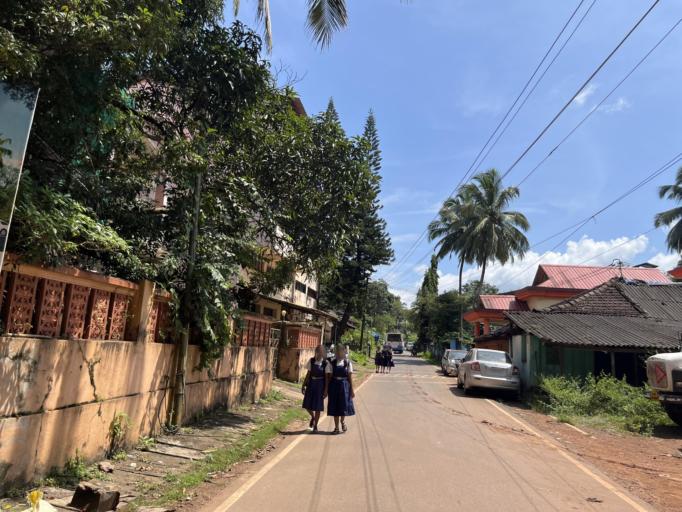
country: IN
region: Goa
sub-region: North Goa
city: Ponda
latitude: 15.3997
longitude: 74.0128
